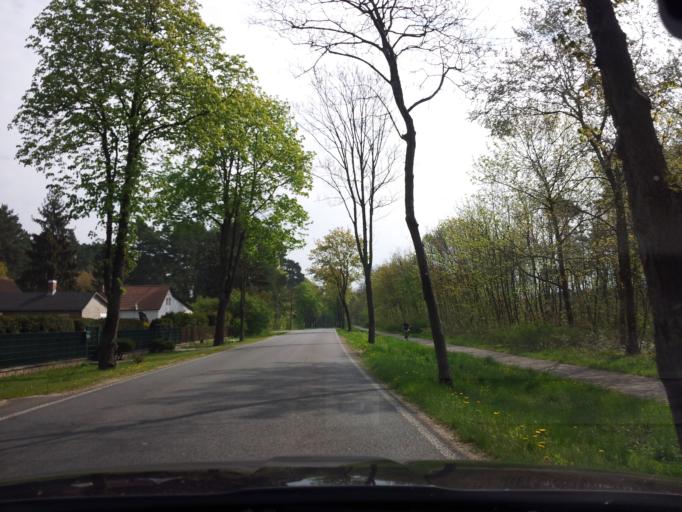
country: DE
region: Brandenburg
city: Rehfelde
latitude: 52.4527
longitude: 13.8758
